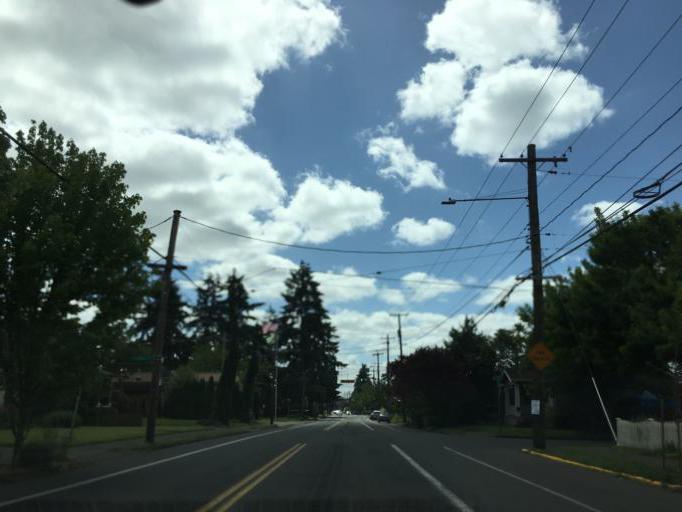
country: US
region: Oregon
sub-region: Multnomah County
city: Lents
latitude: 45.4923
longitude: -122.6090
